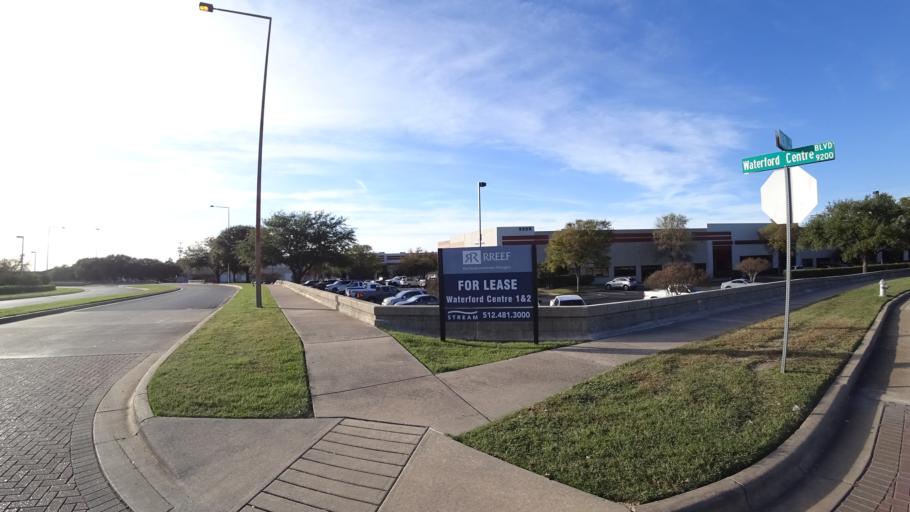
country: US
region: Texas
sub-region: Williamson County
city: Jollyville
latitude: 30.3776
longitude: -97.7284
